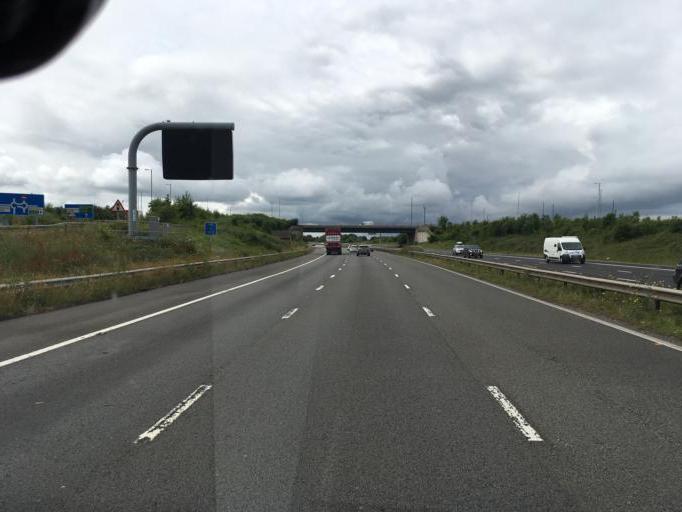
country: GB
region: England
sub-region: Gloucestershire
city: Stonehouse
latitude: 51.7997
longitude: -2.2856
